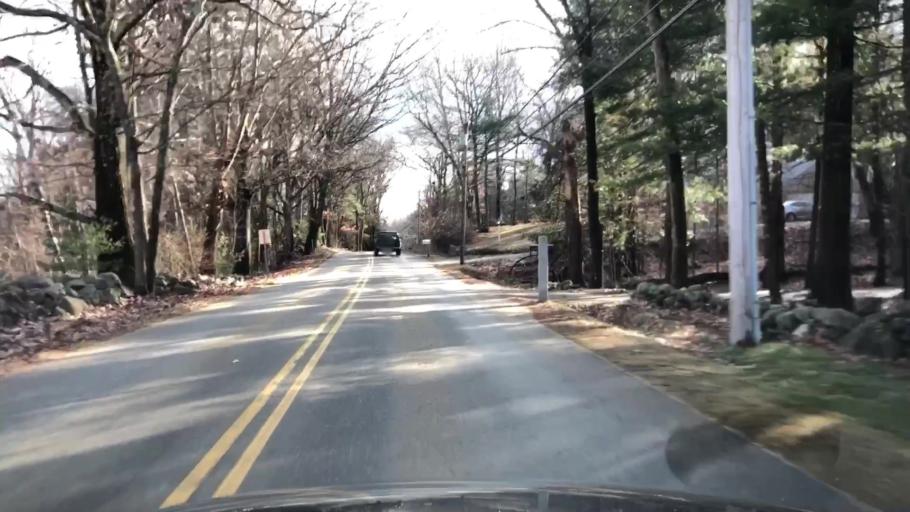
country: US
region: New Hampshire
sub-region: Hillsborough County
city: Mont Vernon
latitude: 42.8868
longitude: -71.6322
